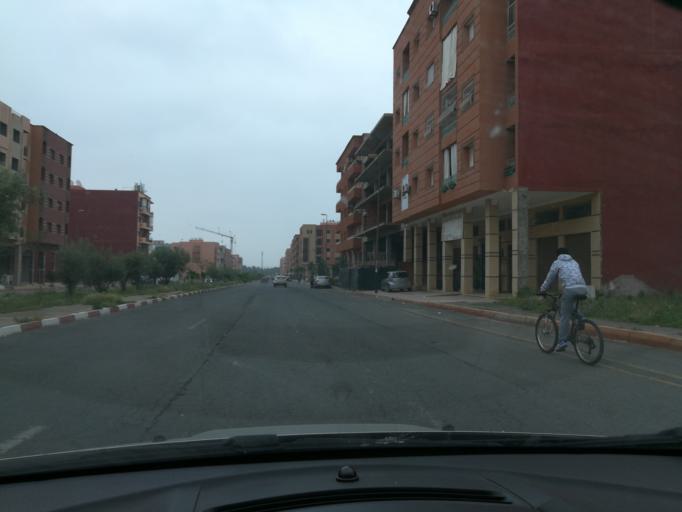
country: MA
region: Marrakech-Tensift-Al Haouz
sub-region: Marrakech
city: Marrakesh
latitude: 31.6737
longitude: -8.0271
